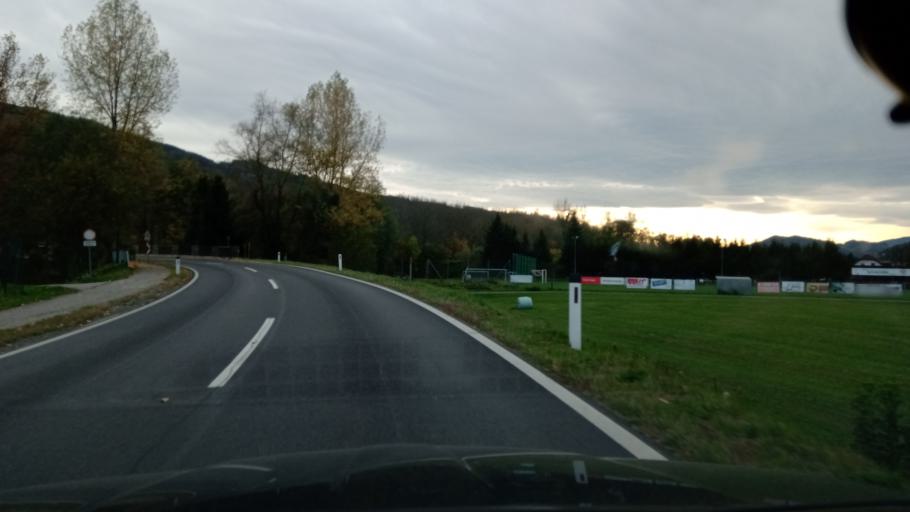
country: AT
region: Styria
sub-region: Politischer Bezirk Leoben
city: Proleb
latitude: 47.3982
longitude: 15.1479
